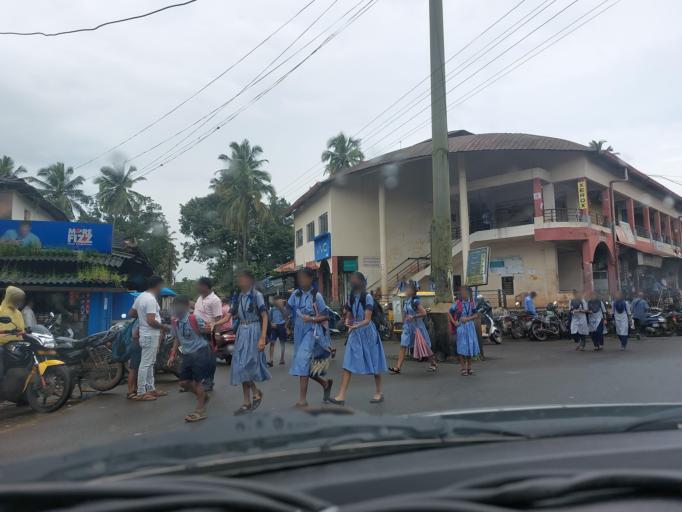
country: IN
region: Goa
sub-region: North Goa
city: Valpoy
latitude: 15.5311
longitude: 74.1372
